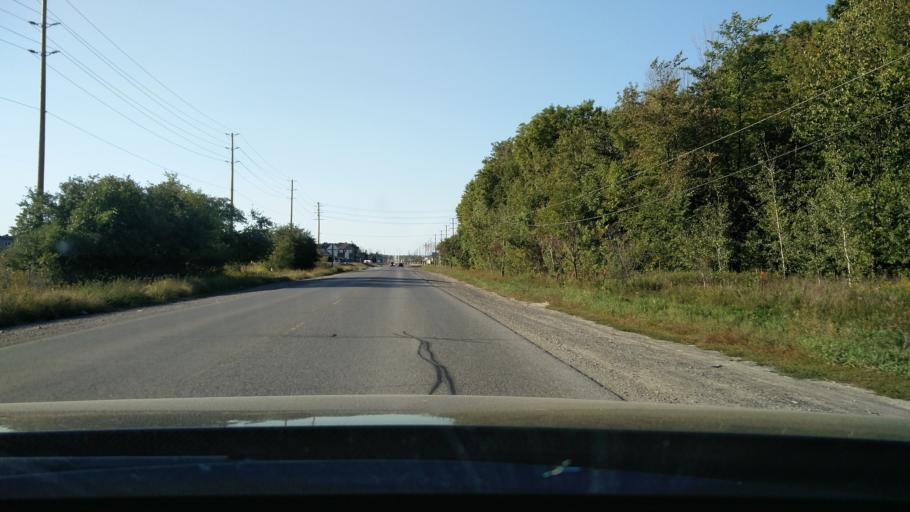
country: CA
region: Ontario
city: Bells Corners
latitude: 45.2375
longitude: -75.7268
